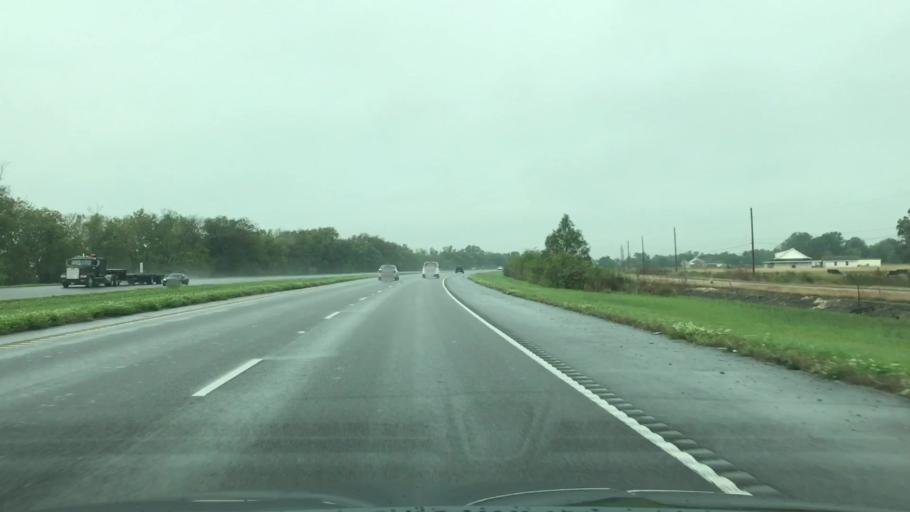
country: US
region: Louisiana
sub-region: Lafourche Parish
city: Raceland
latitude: 29.6920
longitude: -90.5892
